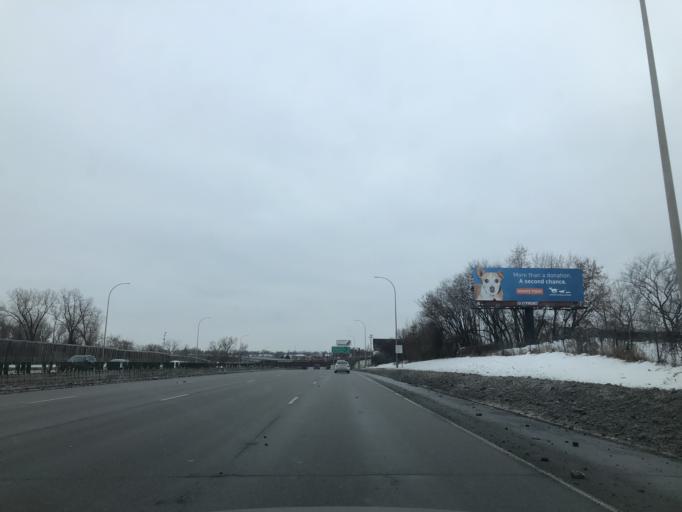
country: US
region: Minnesota
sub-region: Anoka County
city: Columbia Heights
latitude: 45.0364
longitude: -93.2862
